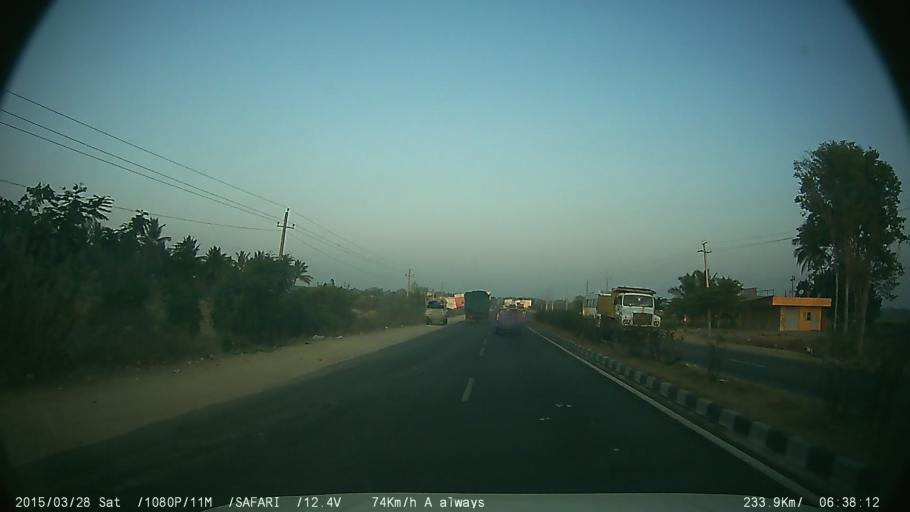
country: IN
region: Karnataka
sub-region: Ramanagara
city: Channapatna
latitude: 12.6466
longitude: 77.1764
